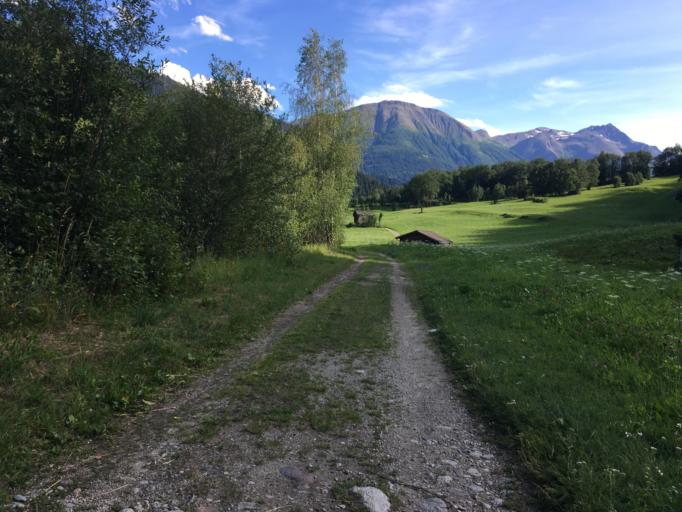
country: CH
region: Valais
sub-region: Goms District
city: Fiesch
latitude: 46.4193
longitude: 8.1408
